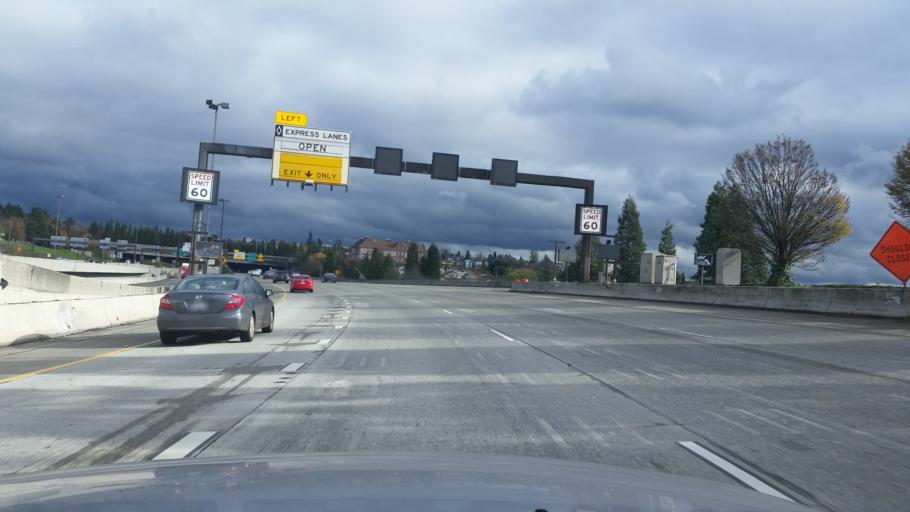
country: US
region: Washington
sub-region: King County
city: Seattle
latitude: 47.5901
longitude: -122.3089
